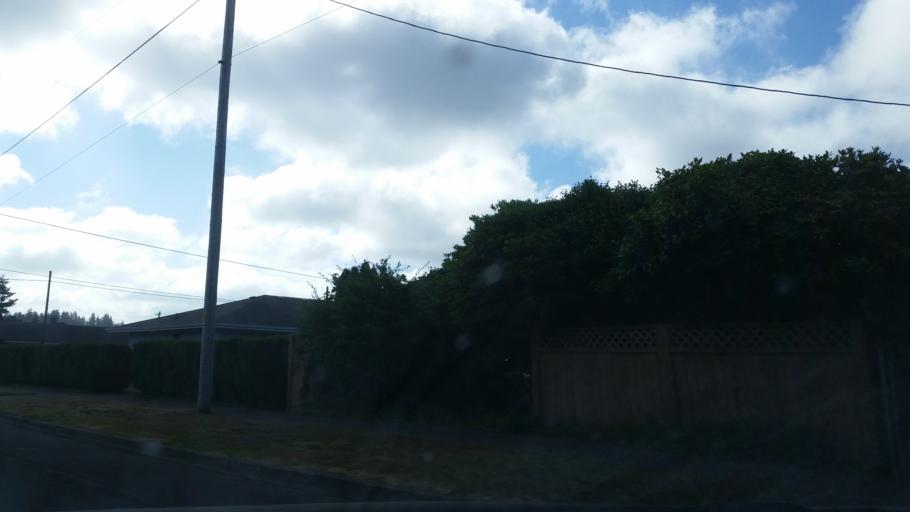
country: US
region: Oregon
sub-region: Clatsop County
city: Astoria
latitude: 46.1813
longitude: -123.8396
